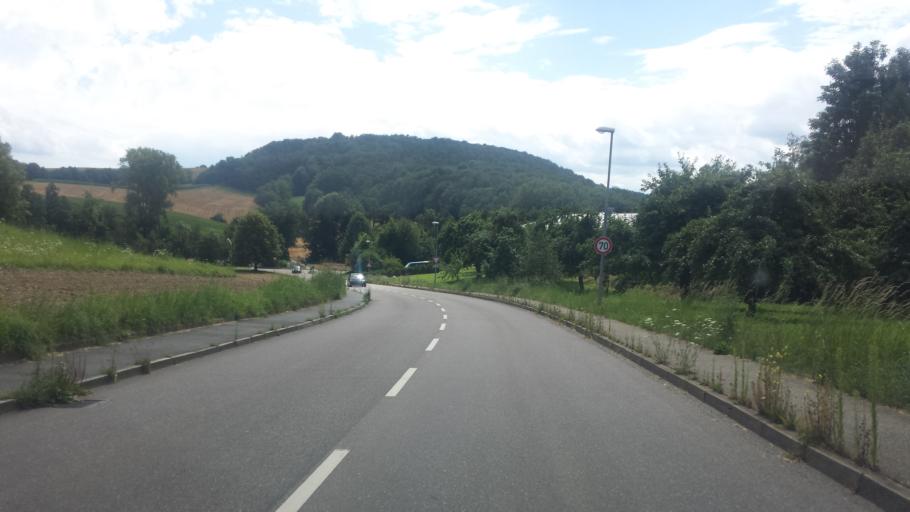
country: DE
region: Baden-Wuerttemberg
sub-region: Karlsruhe Region
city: Horrenberg
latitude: 49.2900
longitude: 8.7685
